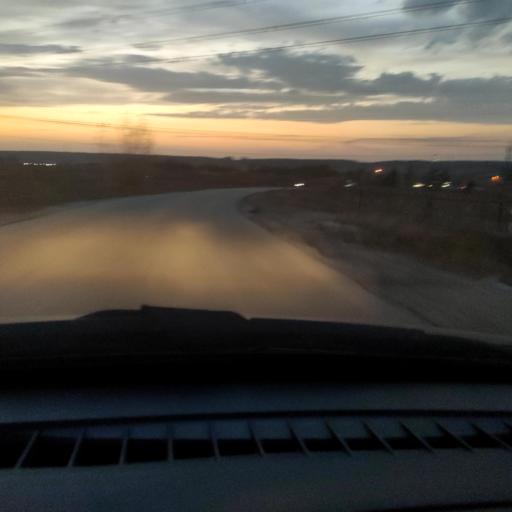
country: RU
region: Samara
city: Zhigulevsk
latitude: 53.5197
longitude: 49.5354
